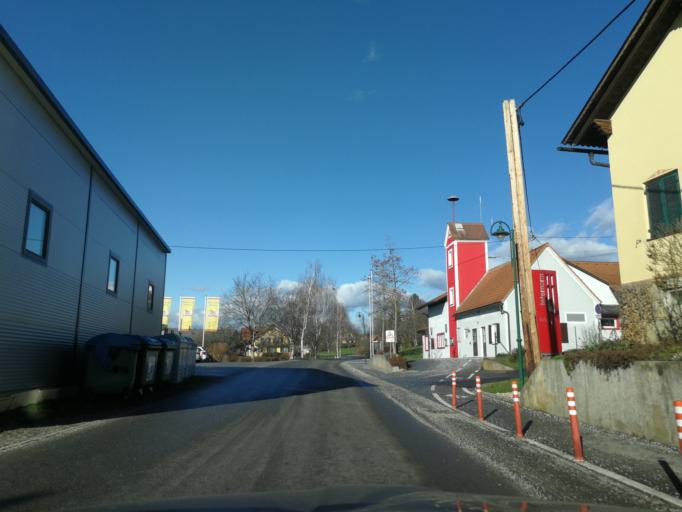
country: AT
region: Styria
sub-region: Politischer Bezirk Weiz
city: Hofstatten an der Raab
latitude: 47.0755
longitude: 15.7466
